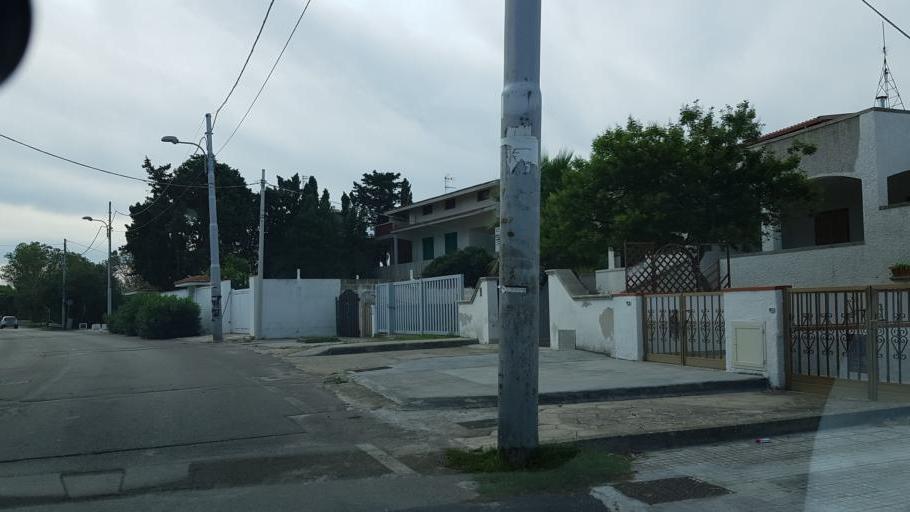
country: IT
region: Apulia
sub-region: Provincia di Lecce
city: Borgagne
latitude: 40.2706
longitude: 18.4291
